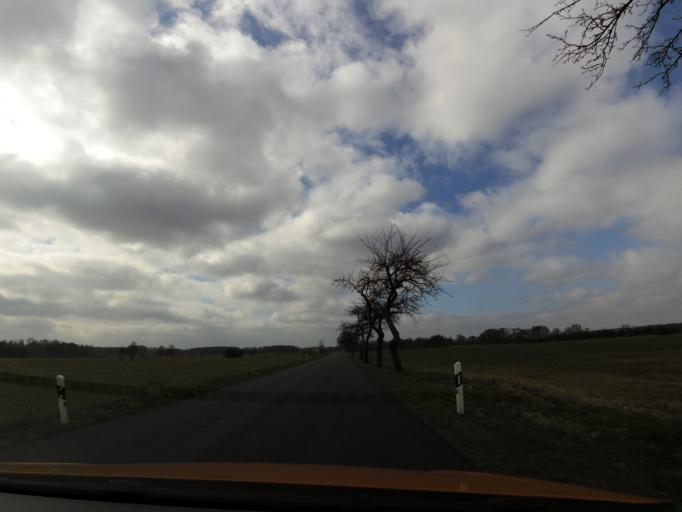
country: DE
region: Brandenburg
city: Rathenow
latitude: 52.6597
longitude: 12.3665
